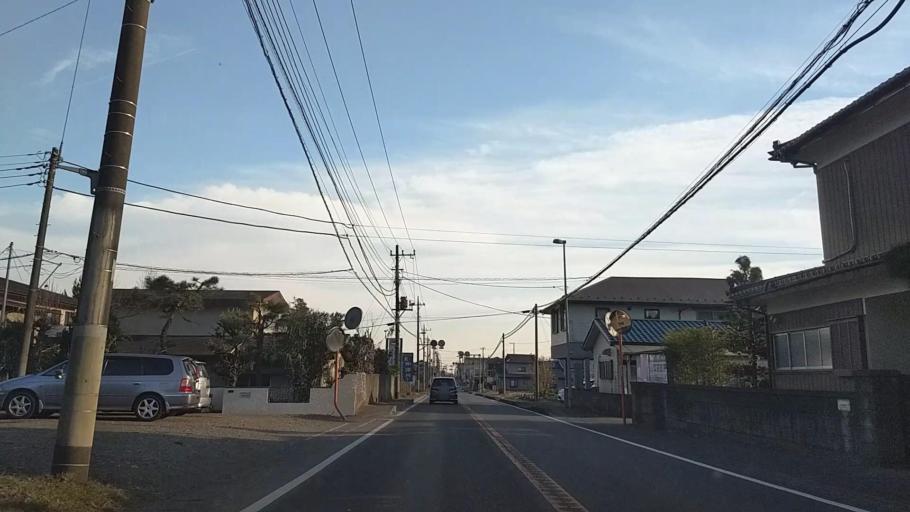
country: JP
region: Kanagawa
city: Zama
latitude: 35.5154
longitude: 139.2976
